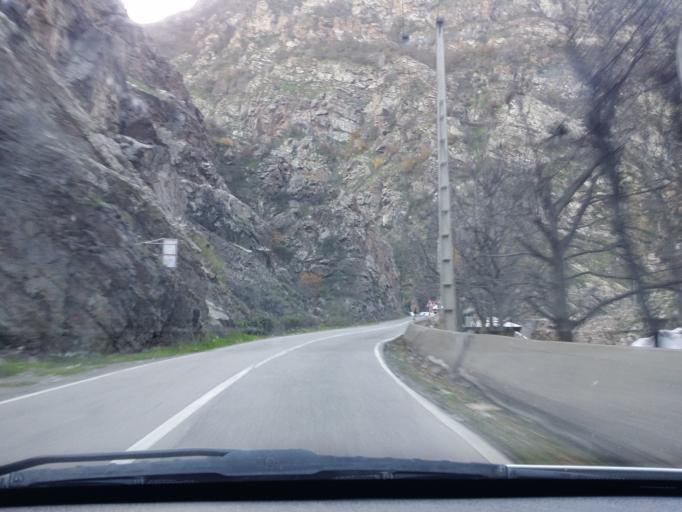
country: IR
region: Mazandaran
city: Chalus
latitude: 36.3017
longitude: 51.2474
